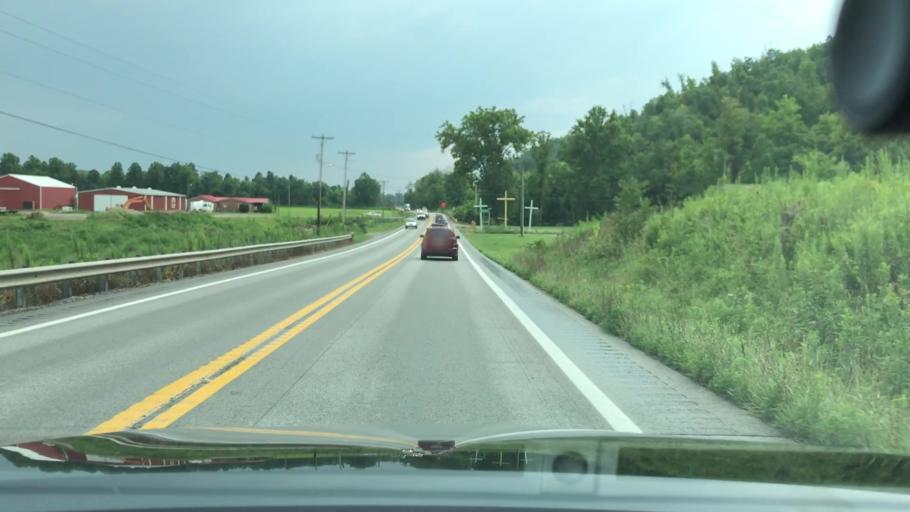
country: US
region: West Virginia
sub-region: Putnam County
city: Buffalo
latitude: 38.6415
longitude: -81.9750
